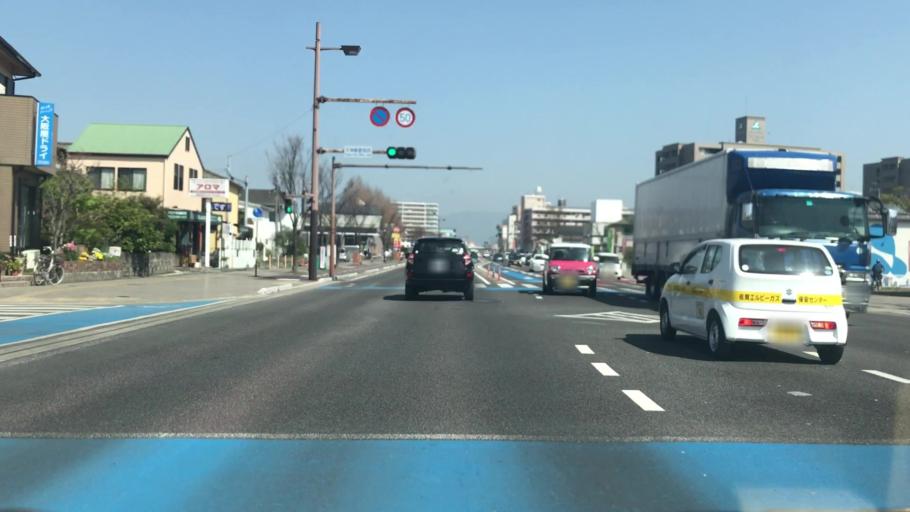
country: JP
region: Saga Prefecture
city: Saga-shi
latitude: 33.2573
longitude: 130.2929
